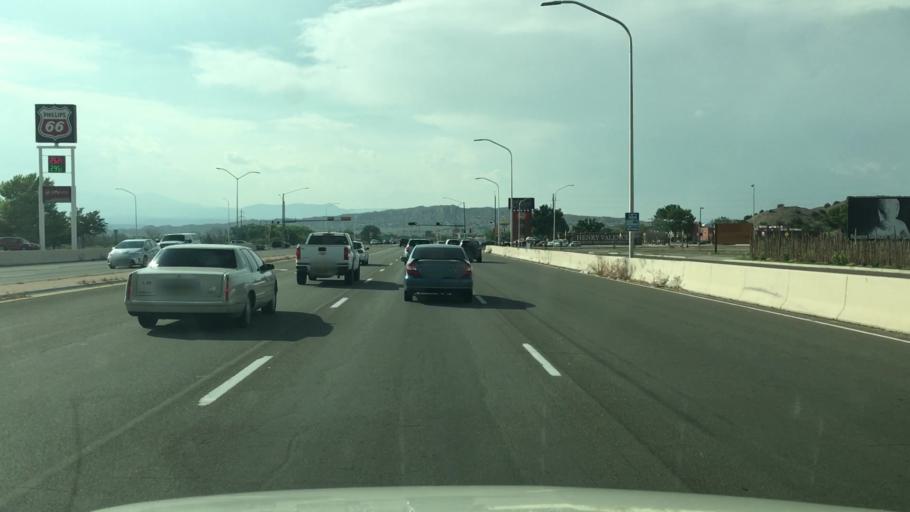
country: US
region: New Mexico
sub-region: Santa Fe County
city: Pojoaque
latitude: 35.8817
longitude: -106.0122
